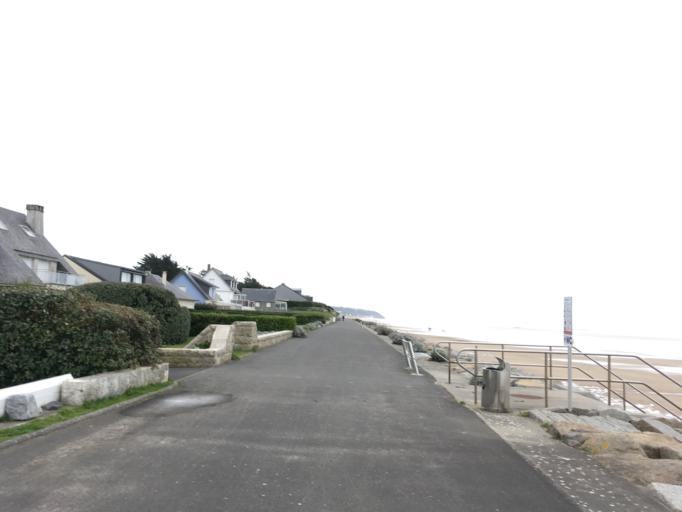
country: FR
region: Lower Normandy
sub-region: Departement de la Manche
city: Saint-Pair-sur-Mer
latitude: 48.7986
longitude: -1.5700
